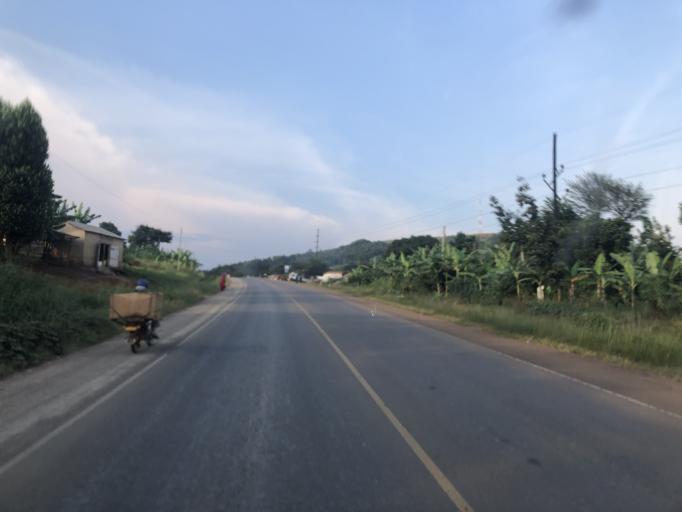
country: UG
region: Central Region
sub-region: Mpigi District
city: Mpigi
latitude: 0.1898
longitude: 32.2933
